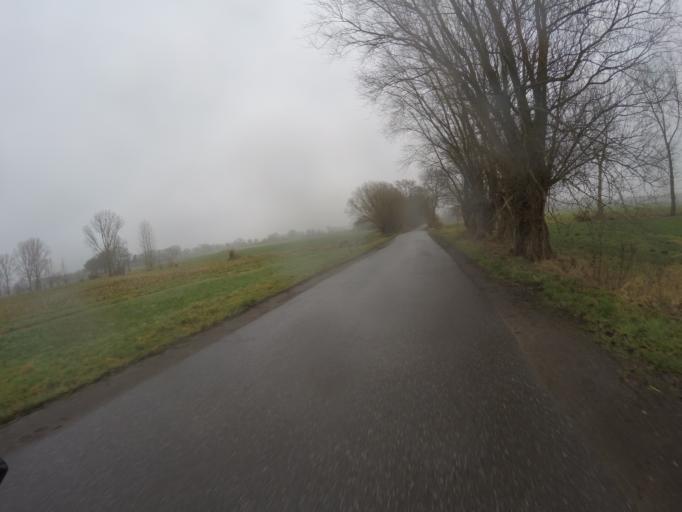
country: DE
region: Schleswig-Holstein
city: Bilsen
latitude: 53.7574
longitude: 9.8978
